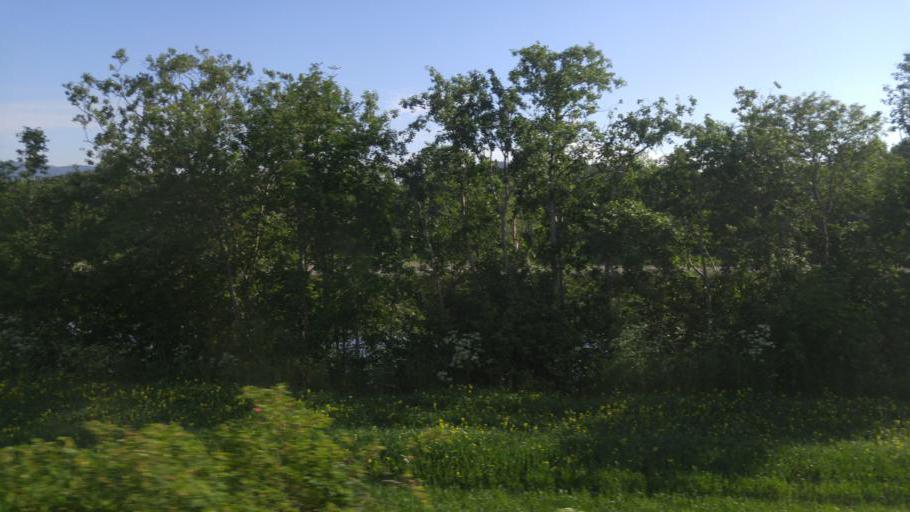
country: NO
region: Nord-Trondelag
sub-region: Stjordal
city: Stjordalshalsen
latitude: 63.4463
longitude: 10.9612
